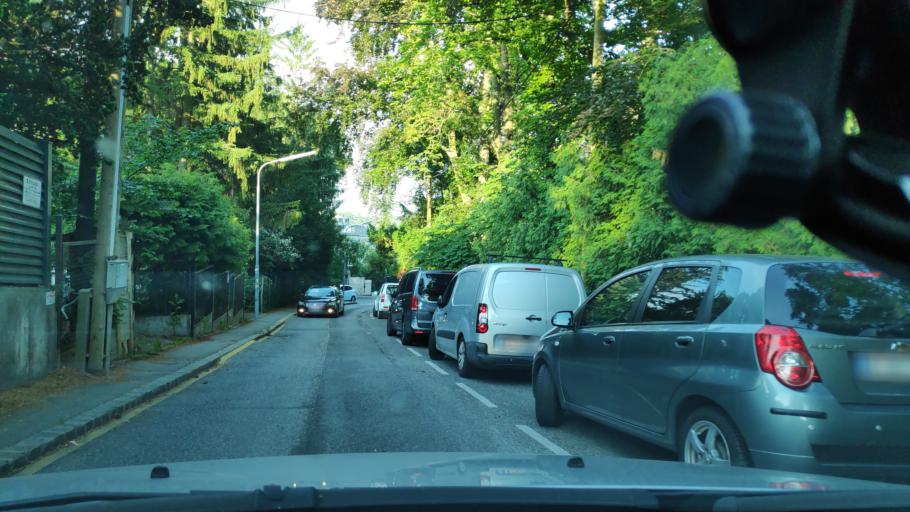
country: AT
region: Lower Austria
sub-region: Politischer Bezirk Wien-Umgebung
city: Klosterneuburg
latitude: 48.2289
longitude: 16.2903
